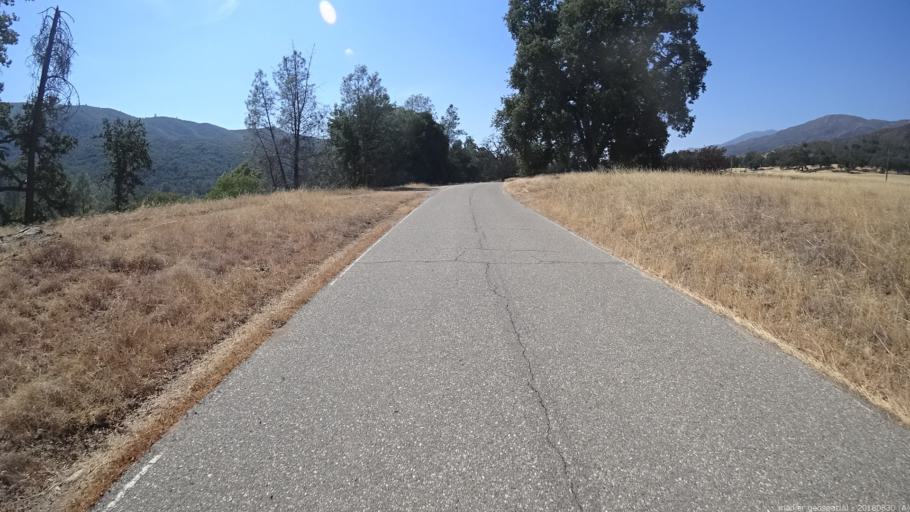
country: US
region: California
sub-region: Monterey County
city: King City
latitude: 36.0681
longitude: -121.3305
